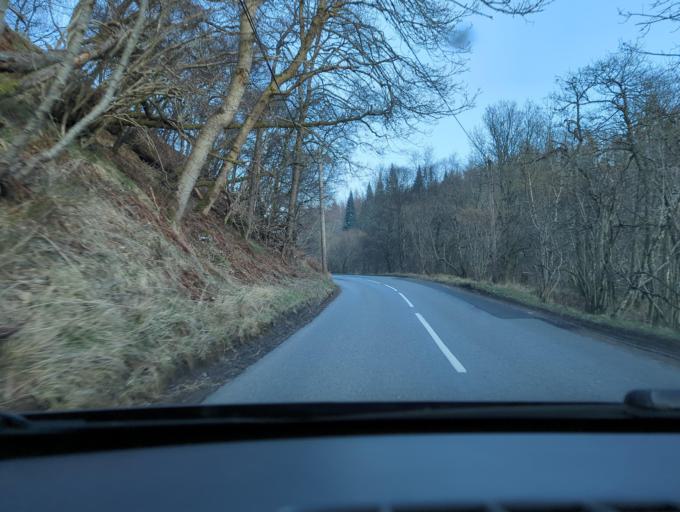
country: GB
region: Scotland
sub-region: Perth and Kinross
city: Methven
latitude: 56.5369
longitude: -3.6765
